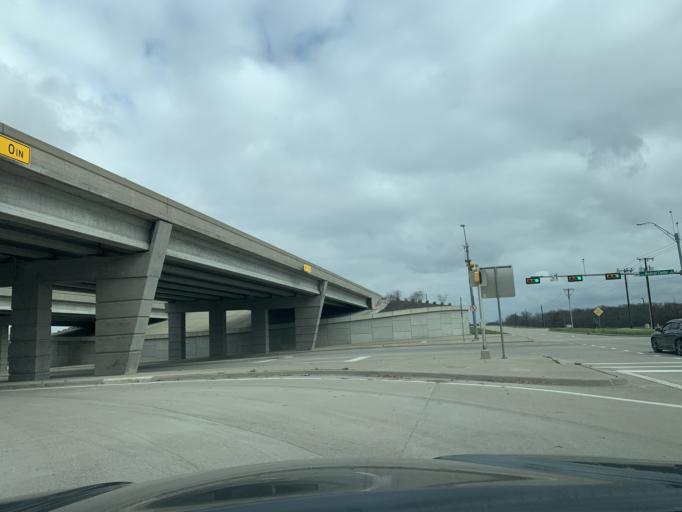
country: US
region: Texas
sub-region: Collin County
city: Fairview
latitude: 33.1620
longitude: -96.6363
